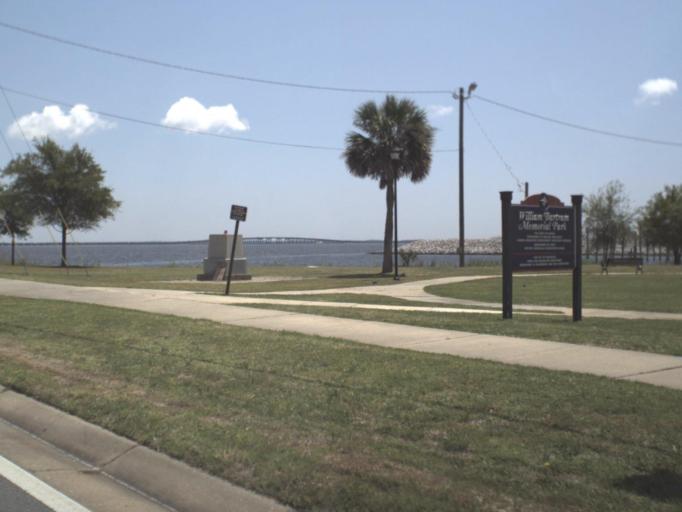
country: US
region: Florida
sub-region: Escambia County
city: Pensacola
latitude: 30.4083
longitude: -87.2095
